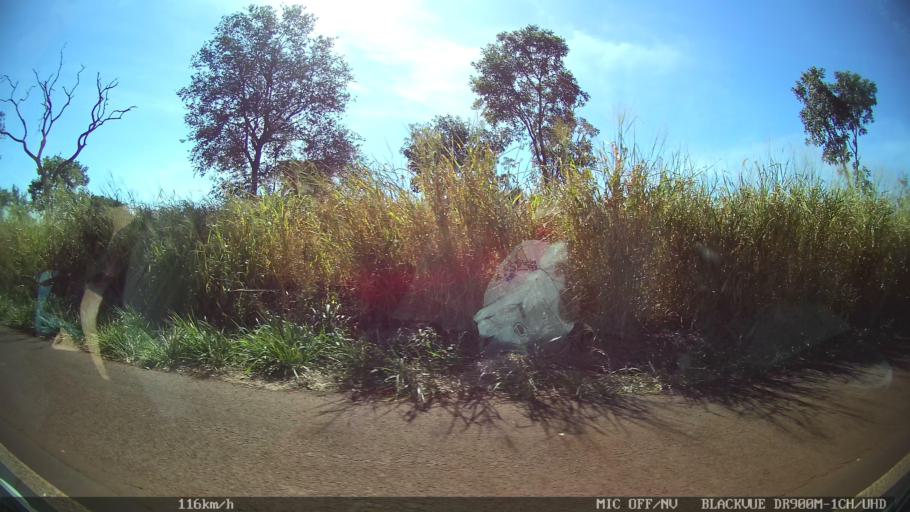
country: BR
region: Sao Paulo
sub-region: Guaira
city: Guaira
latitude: -20.4435
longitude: -48.3224
